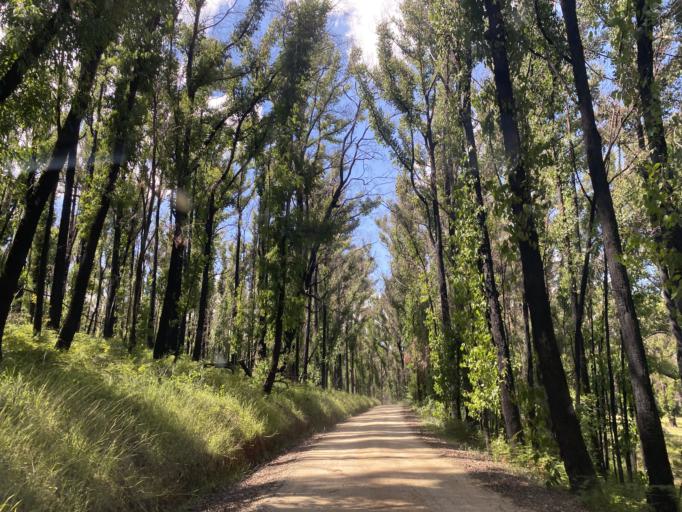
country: AU
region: Victoria
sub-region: Cardinia
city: Gembrook
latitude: -37.9826
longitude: 145.6546
